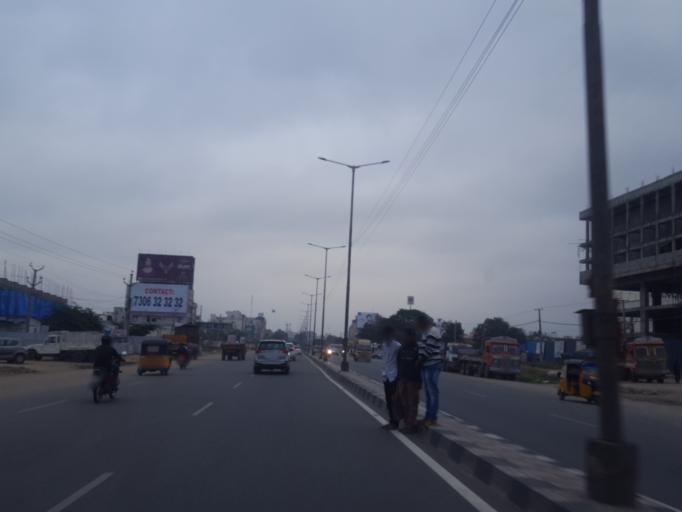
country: IN
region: Telangana
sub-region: Medak
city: Serilingampalle
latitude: 17.5113
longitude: 78.2949
